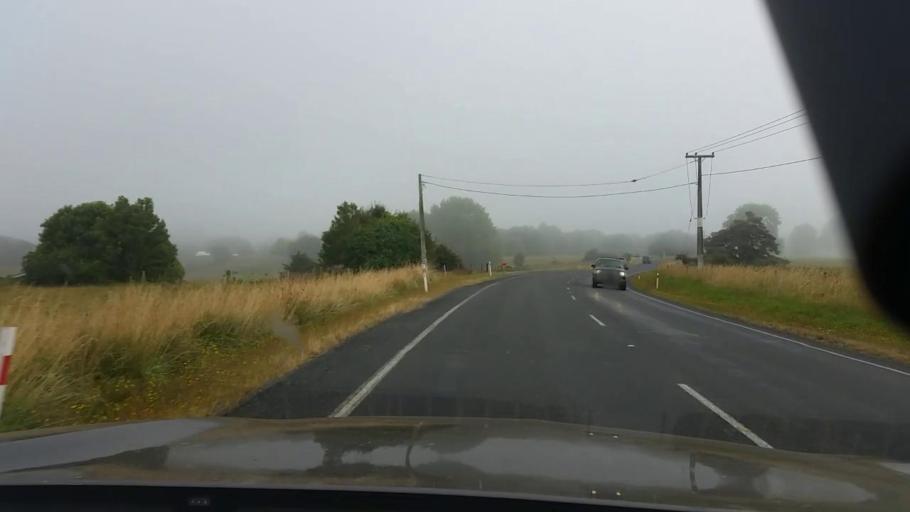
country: NZ
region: Waikato
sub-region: Hamilton City
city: Hamilton
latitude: -37.6456
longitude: 175.2960
